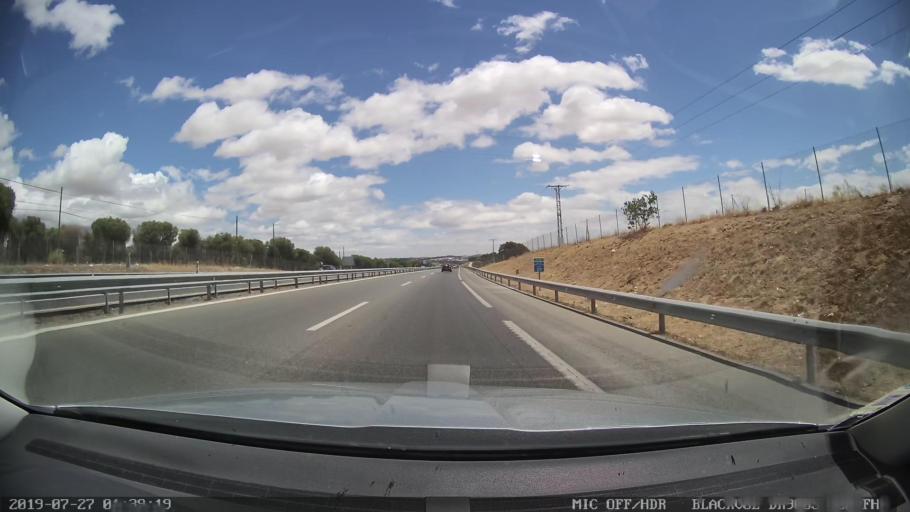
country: ES
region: Madrid
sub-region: Provincia de Madrid
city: Navalcarnero
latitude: 40.2965
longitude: -3.9640
